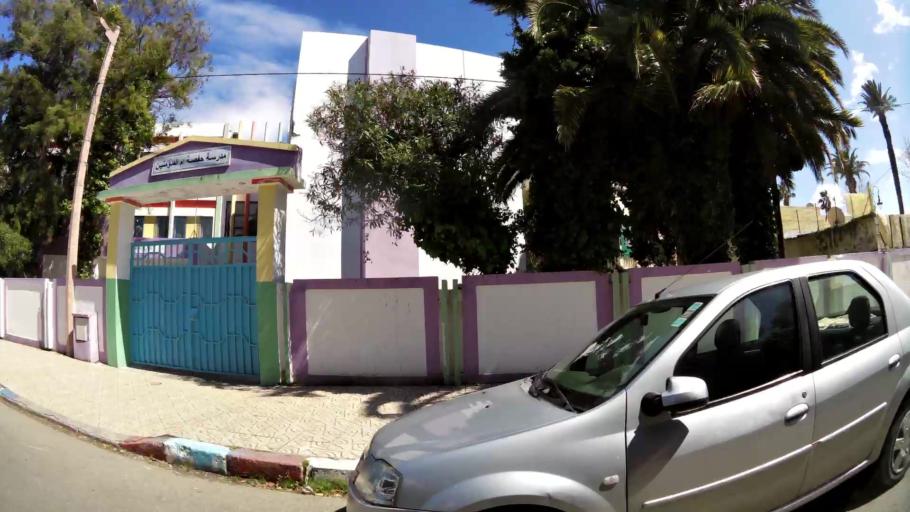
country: MA
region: Tanger-Tetouan
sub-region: Tanger-Assilah
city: Tangier
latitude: 35.7885
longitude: -5.8195
